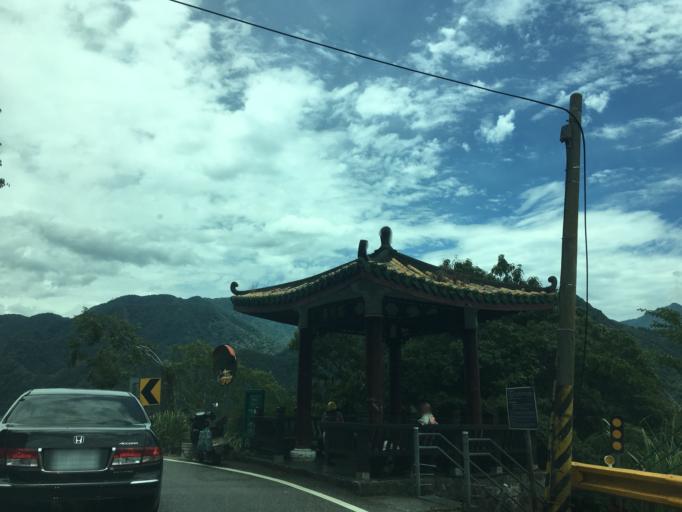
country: TW
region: Taiwan
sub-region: Hualien
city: Hualian
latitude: 24.1902
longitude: 121.4856
